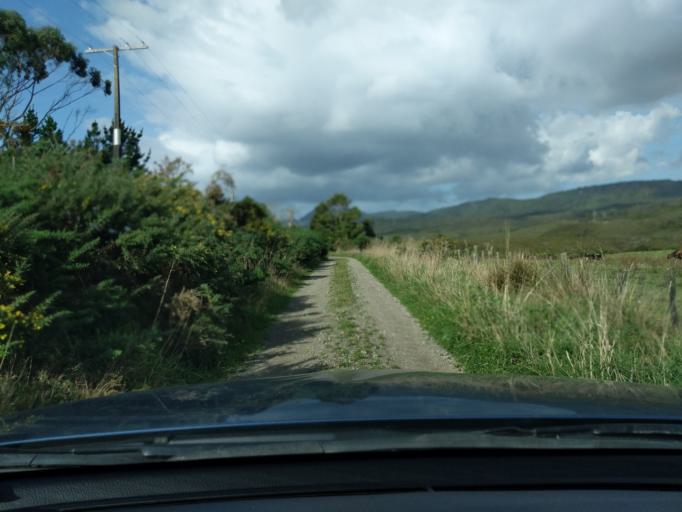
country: NZ
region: Tasman
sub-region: Tasman District
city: Takaka
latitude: -40.6513
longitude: 172.4759
